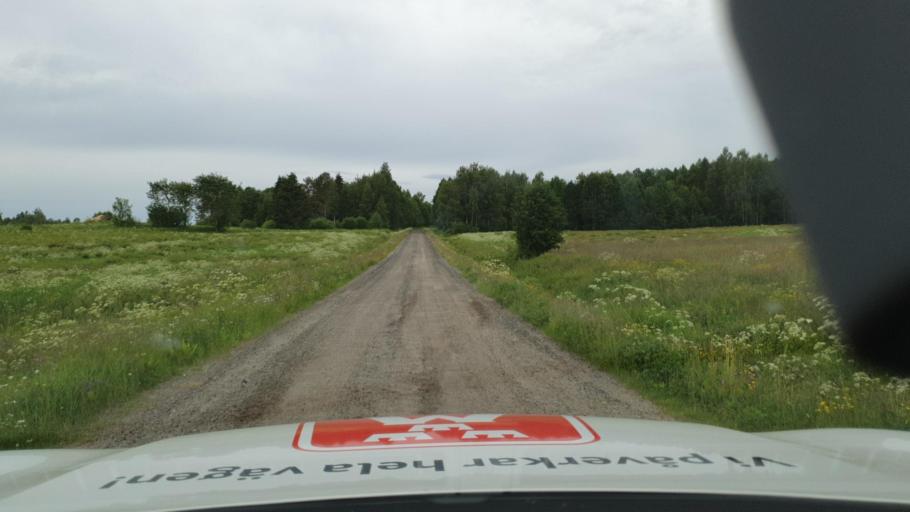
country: SE
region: Vaesterbotten
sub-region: Robertsfors Kommun
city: Robertsfors
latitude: 64.2044
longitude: 20.6999
